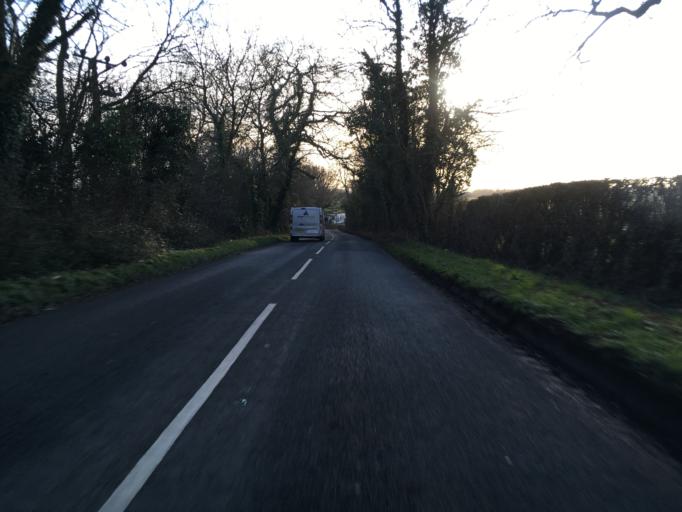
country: GB
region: England
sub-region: Warwickshire
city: Stratford-upon-Avon
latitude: 52.2246
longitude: -1.7343
